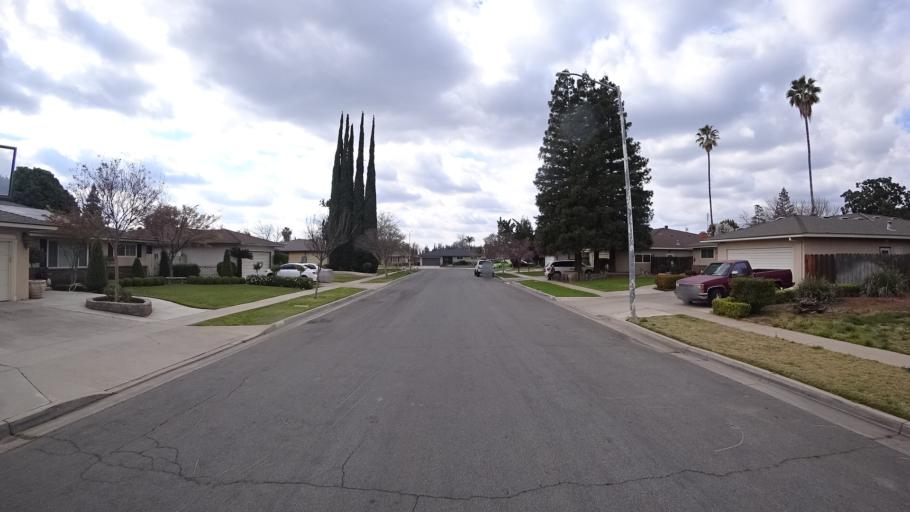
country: US
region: California
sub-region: Fresno County
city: Clovis
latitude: 36.8348
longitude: -119.7755
